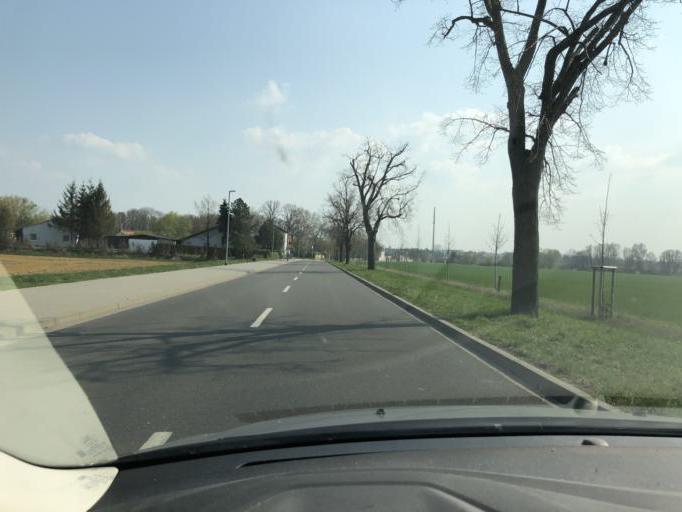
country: DE
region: Saxony-Anhalt
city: Grobers
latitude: 51.4406
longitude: 12.1154
